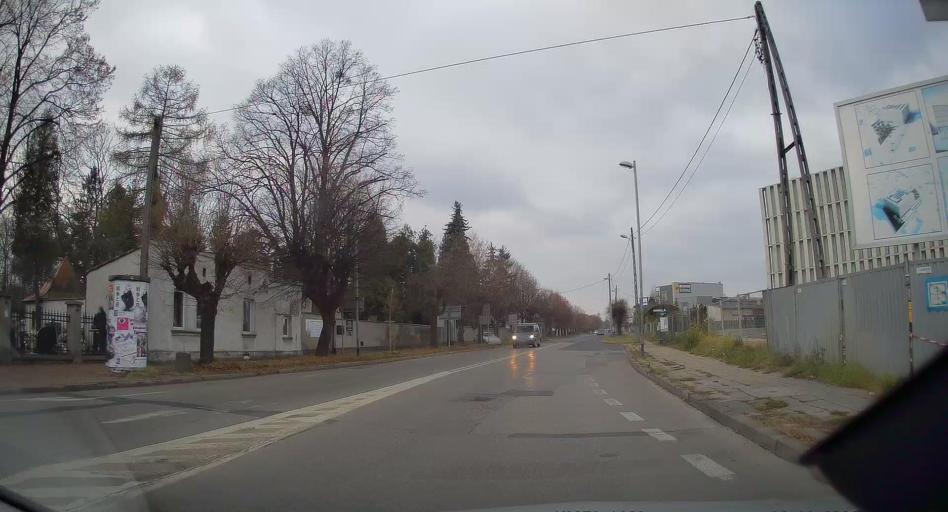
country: PL
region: Silesian Voivodeship
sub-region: Czestochowa
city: Czestochowa
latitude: 50.8193
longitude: 19.0870
